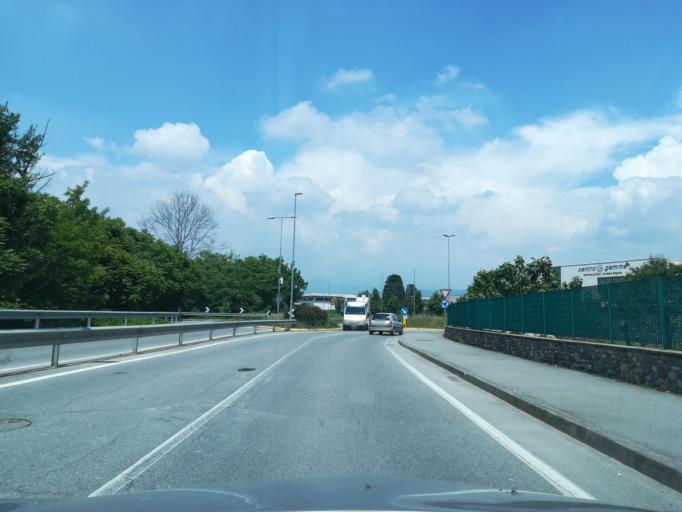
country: IT
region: Lombardy
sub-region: Provincia di Bergamo
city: Grassobbio
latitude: 45.6597
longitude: 9.7433
